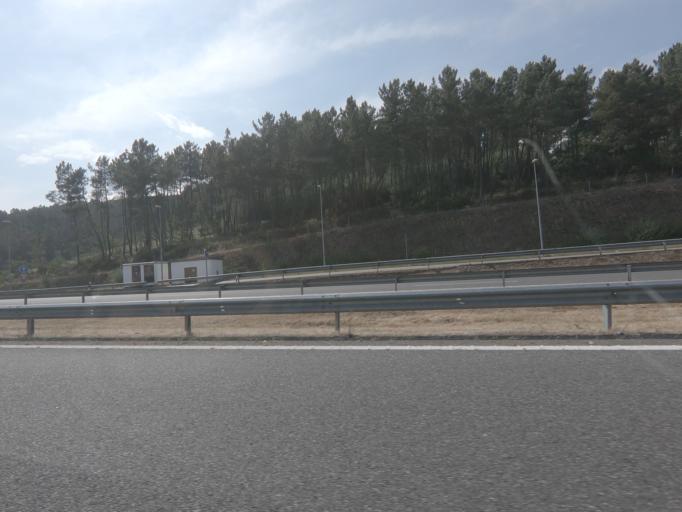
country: ES
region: Galicia
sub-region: Provincia de Ourense
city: Cenlle
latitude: 42.3123
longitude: -8.0951
